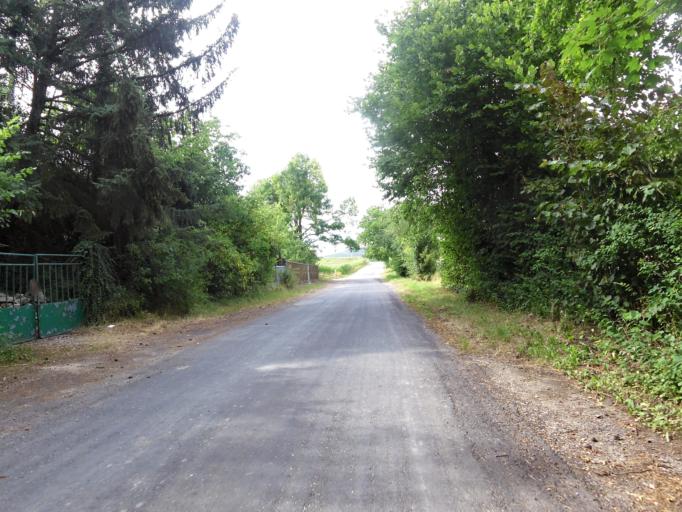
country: DE
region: Bavaria
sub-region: Regierungsbezirk Unterfranken
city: Randersacker
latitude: 49.7427
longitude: 9.9816
